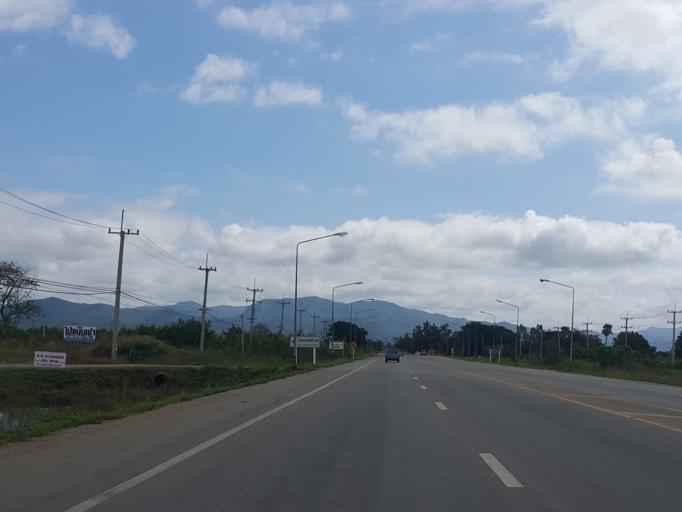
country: TH
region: Chiang Mai
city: San Kamphaeng
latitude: 18.7148
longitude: 99.1201
